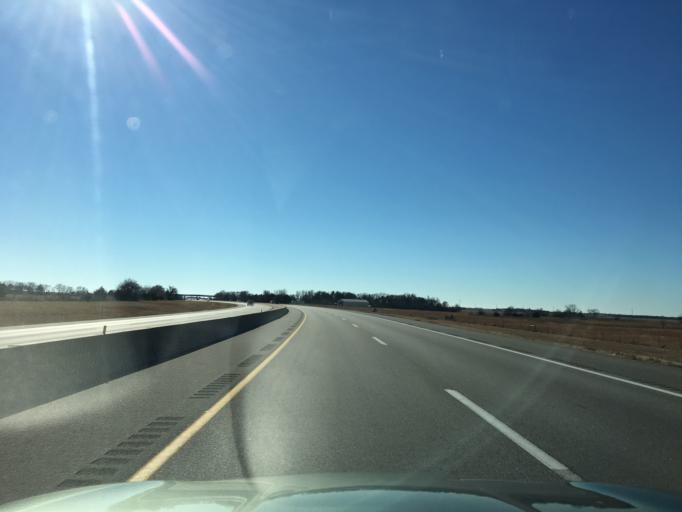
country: US
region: Kansas
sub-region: Sumner County
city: Wellington
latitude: 37.3257
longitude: -97.3388
